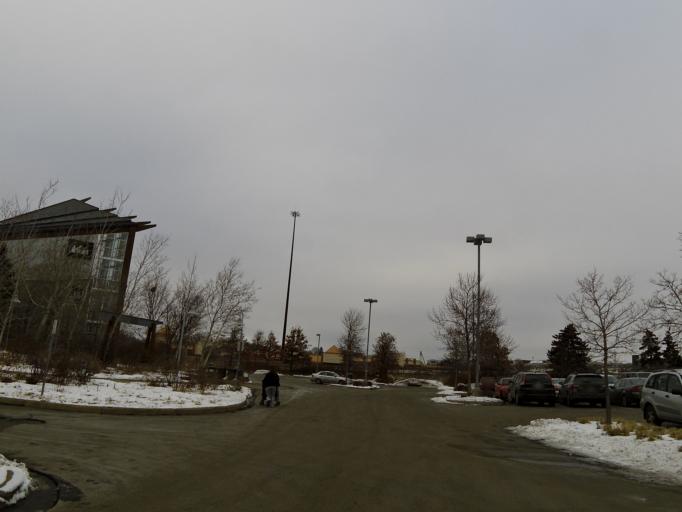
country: US
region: Minnesota
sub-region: Hennepin County
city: Bloomington
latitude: 44.8606
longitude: -93.2903
